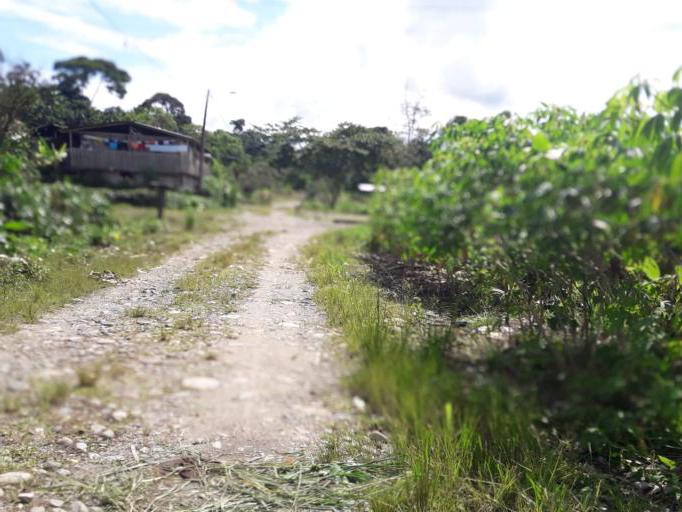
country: EC
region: Napo
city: Tena
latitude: -0.9553
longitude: -77.8251
